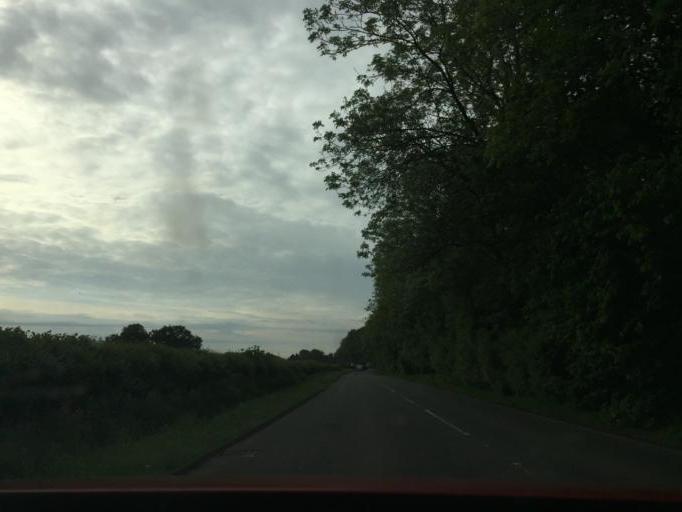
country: GB
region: England
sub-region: Leicestershire
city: Sapcote
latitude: 52.4685
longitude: -1.3093
